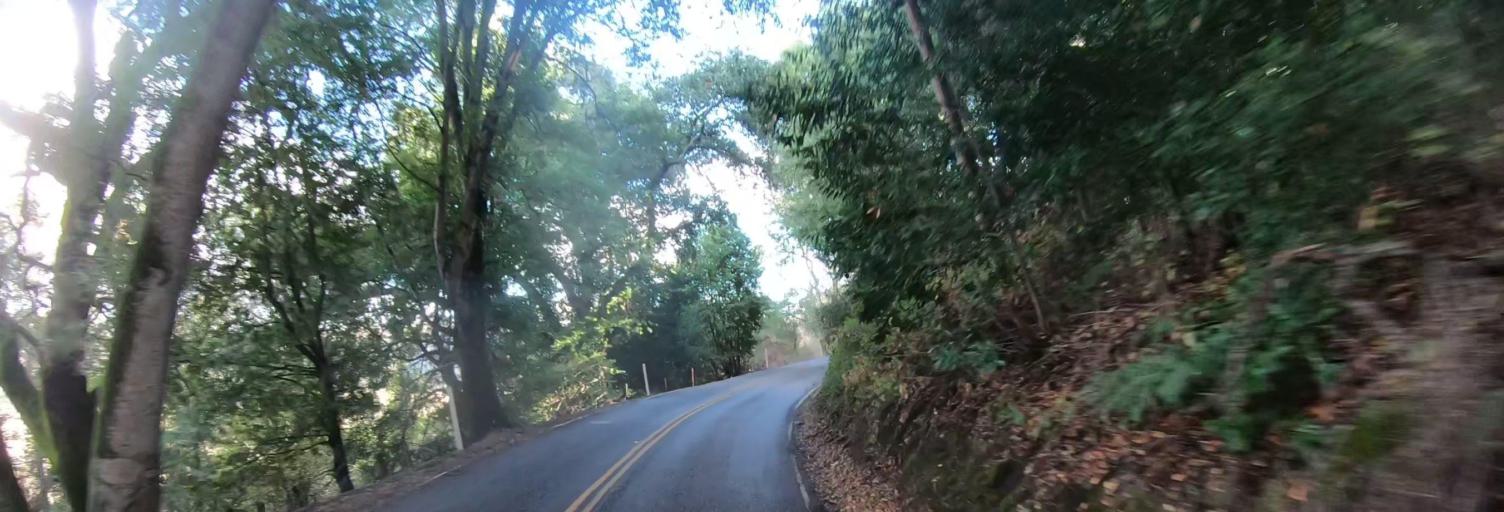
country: US
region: California
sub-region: Santa Clara County
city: East Foothills
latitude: 37.3491
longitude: -121.7300
